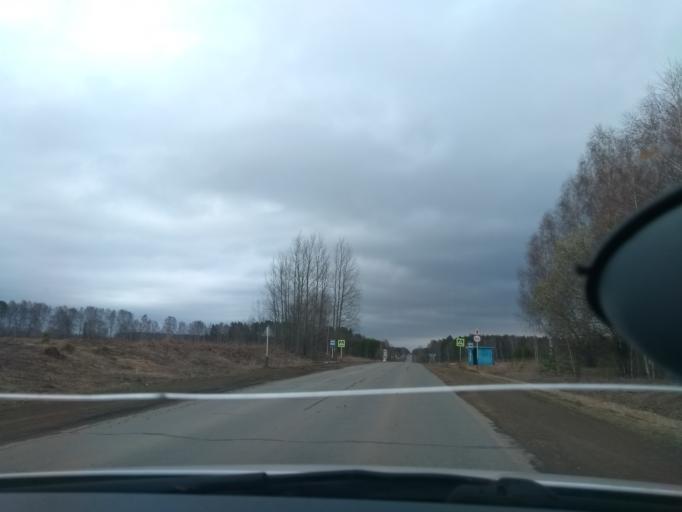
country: RU
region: Perm
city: Orda
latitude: 57.3416
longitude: 56.7840
